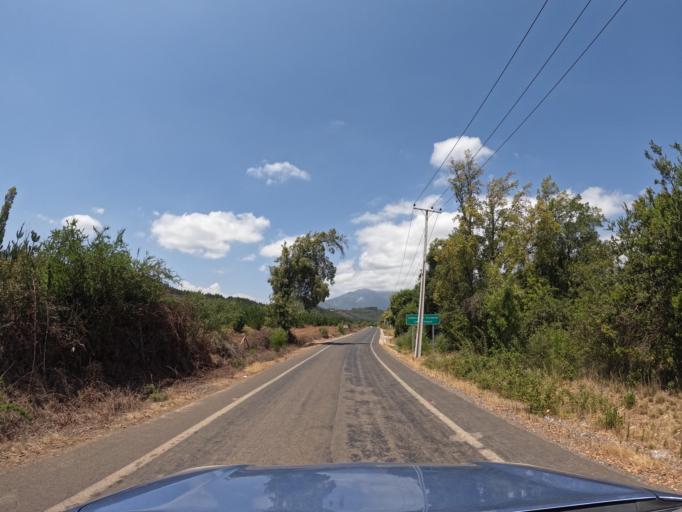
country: CL
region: Maule
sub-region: Provincia de Curico
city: Molina
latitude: -35.1784
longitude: -71.1086
